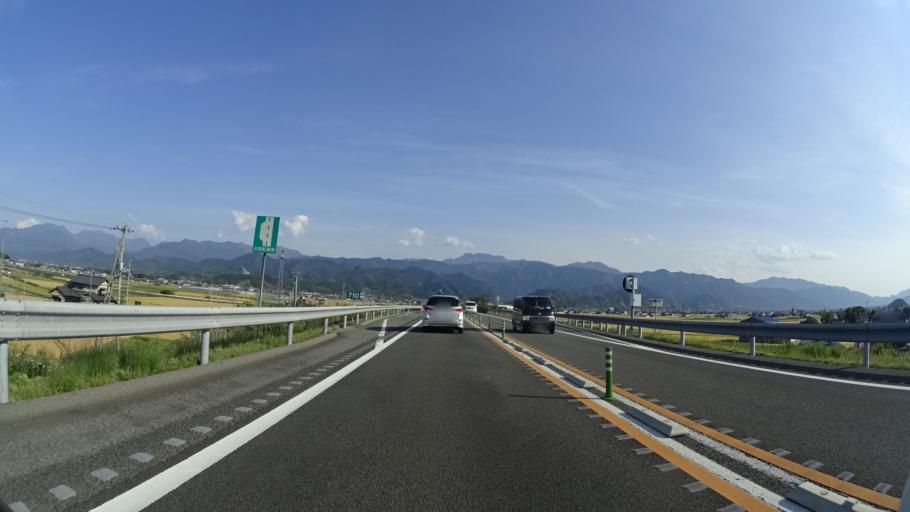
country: JP
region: Ehime
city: Saijo
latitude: 33.9094
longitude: 133.0735
